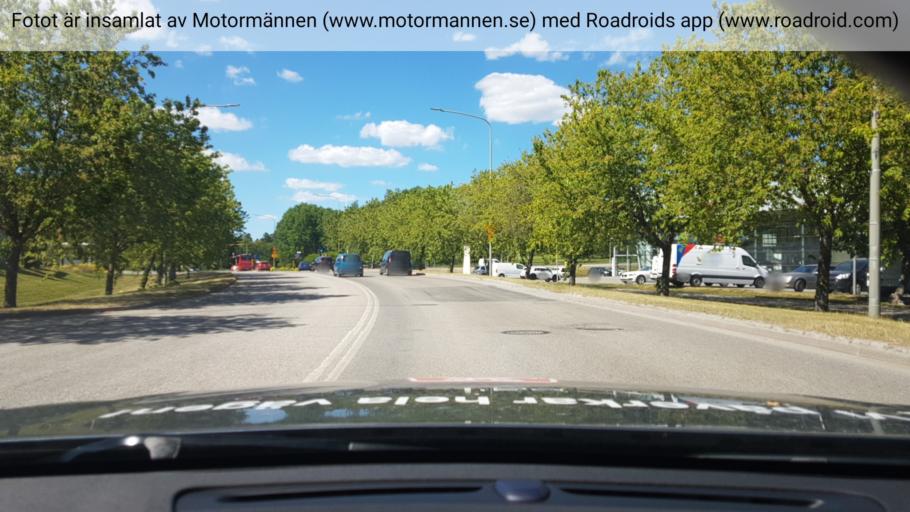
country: SE
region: Stockholm
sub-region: Jarfalla Kommun
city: Jakobsberg
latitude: 59.3911
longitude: 17.8714
